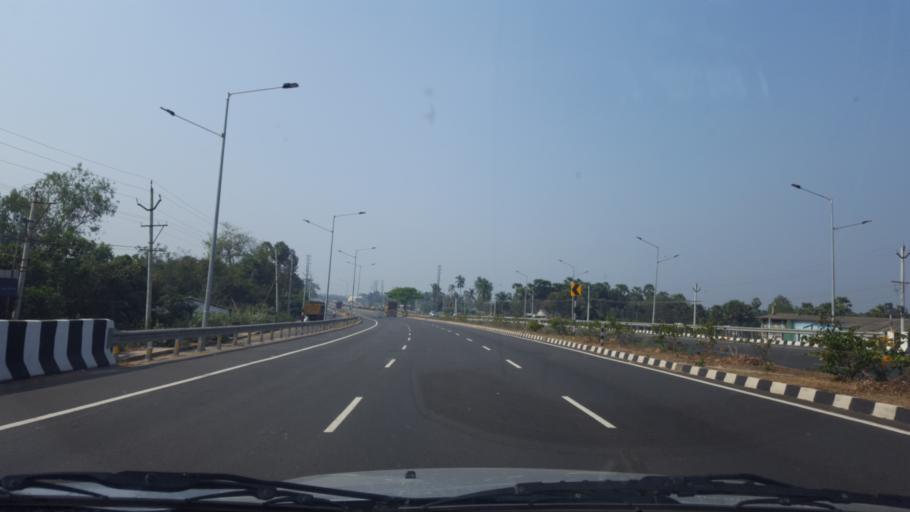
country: IN
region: Andhra Pradesh
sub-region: Vizianagaram District
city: Vizianagaram
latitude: 18.0277
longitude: 83.4922
